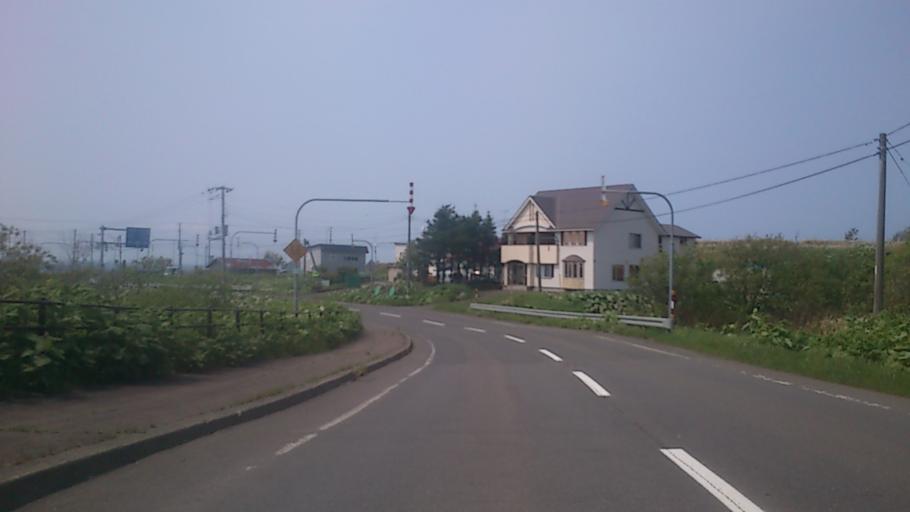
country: JP
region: Hokkaido
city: Nemuro
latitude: 43.2807
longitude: 145.5086
